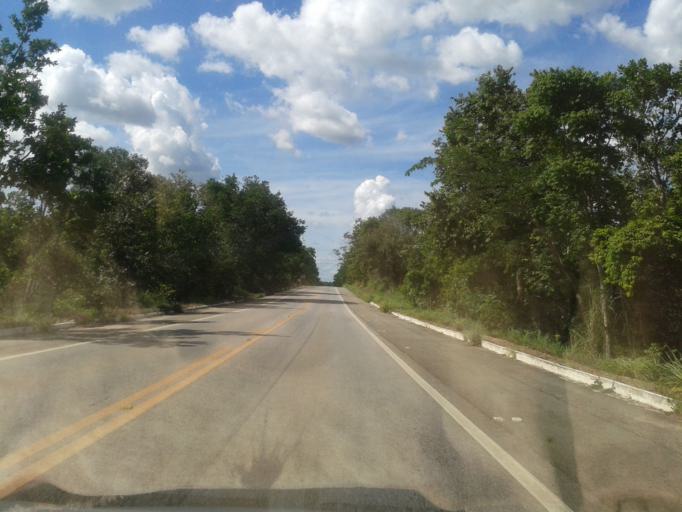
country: BR
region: Goias
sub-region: Itapuranga
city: Itapuranga
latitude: -15.5342
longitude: -50.2925
